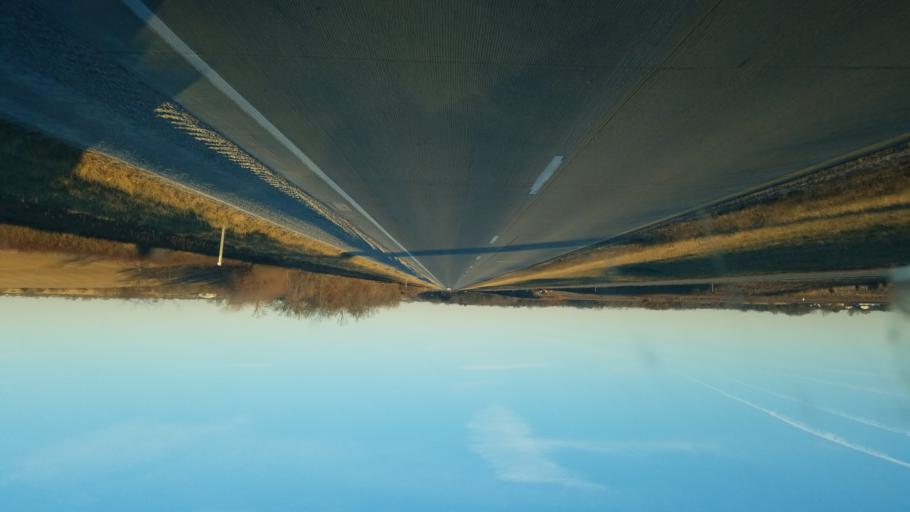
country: US
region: Iowa
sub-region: Wapello County
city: Ottumwa
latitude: 41.0021
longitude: -92.2640
